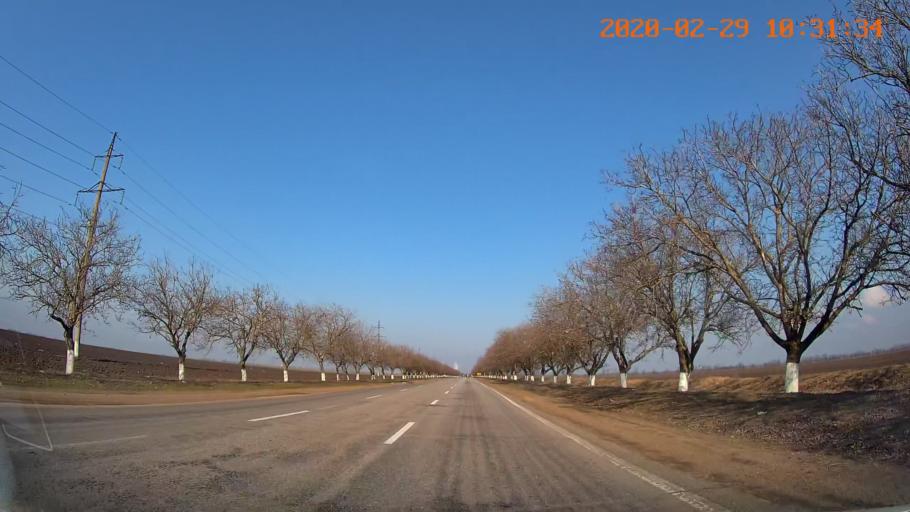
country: UA
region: Odessa
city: Velykoploske
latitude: 46.9501
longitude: 29.5625
